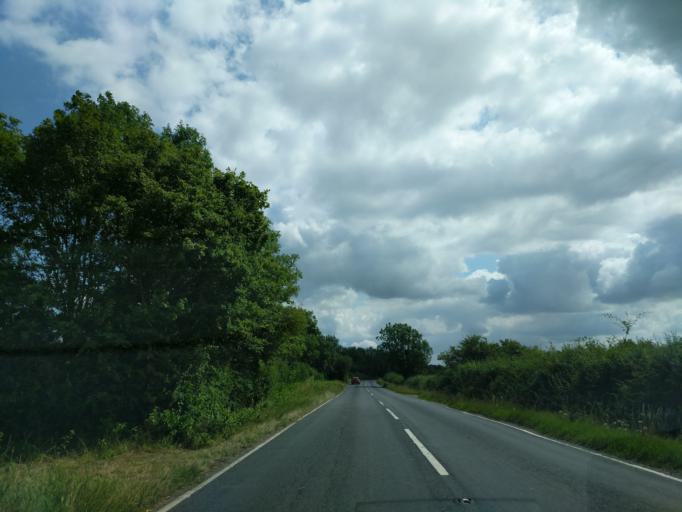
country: GB
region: England
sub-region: Cambridgeshire
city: Isleham
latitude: 52.3063
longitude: 0.4247
